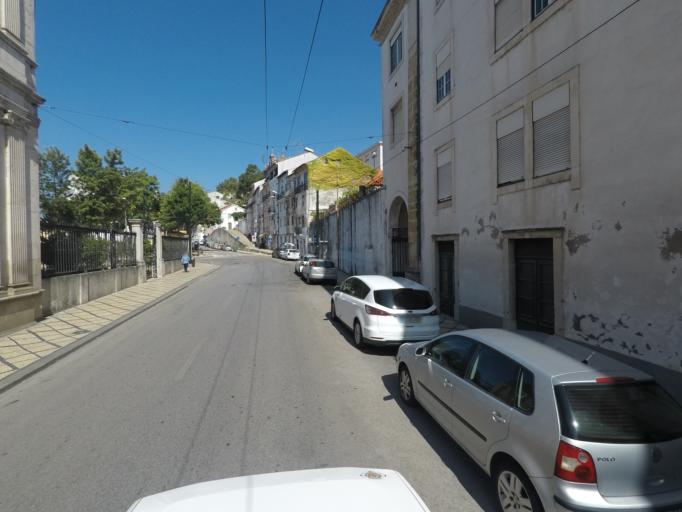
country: PT
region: Coimbra
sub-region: Coimbra
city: Coimbra
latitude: 40.2145
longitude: -8.4320
